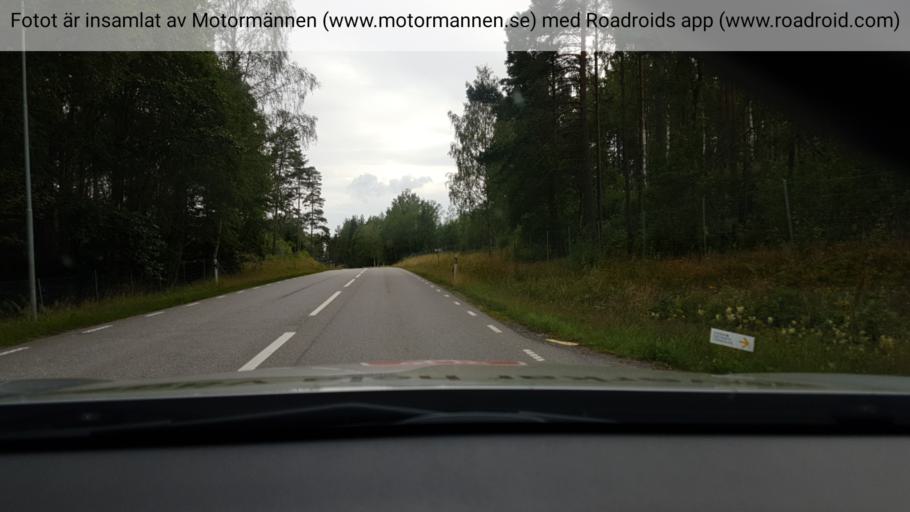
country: SE
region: Vaestra Goetaland
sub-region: Bengtsfors Kommun
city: Billingsfors
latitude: 58.9711
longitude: 12.2386
